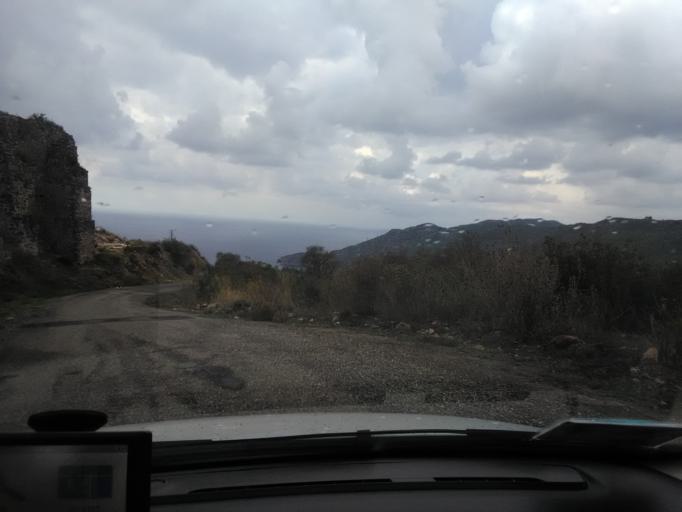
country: TR
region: Antalya
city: Gazipasa
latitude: 36.1546
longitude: 32.4276
